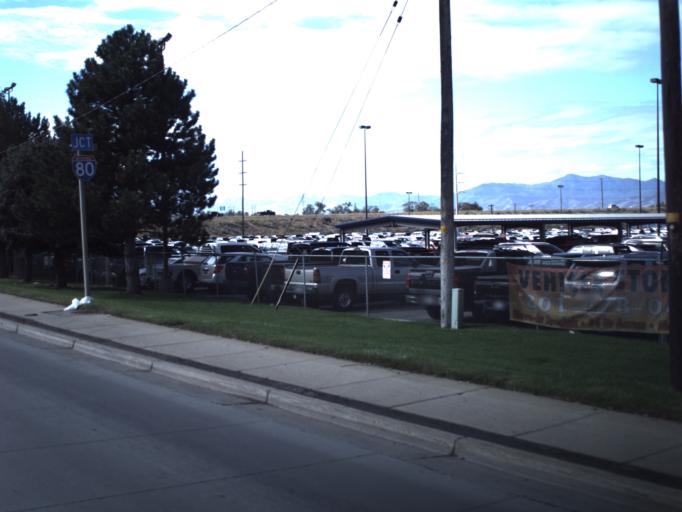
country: US
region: Utah
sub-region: Salt Lake County
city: Salt Lake City
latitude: 40.7690
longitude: -111.9393
